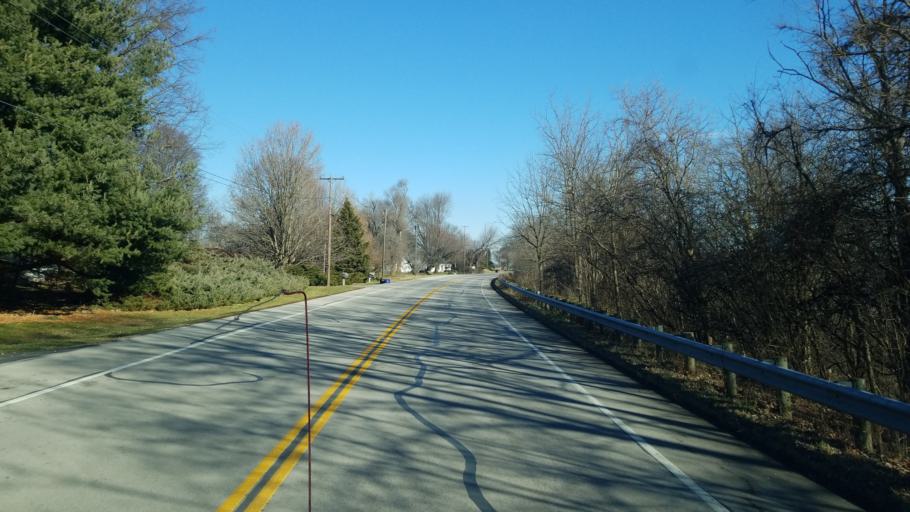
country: US
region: Ohio
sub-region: Lucas County
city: Whitehouse
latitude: 41.4636
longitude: -83.7789
